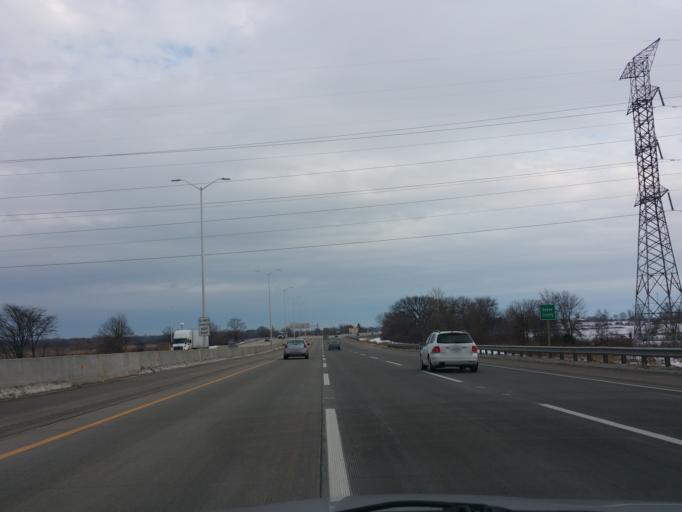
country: US
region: Illinois
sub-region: Winnebago County
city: Cherry Valley
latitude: 42.2471
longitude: -88.9419
